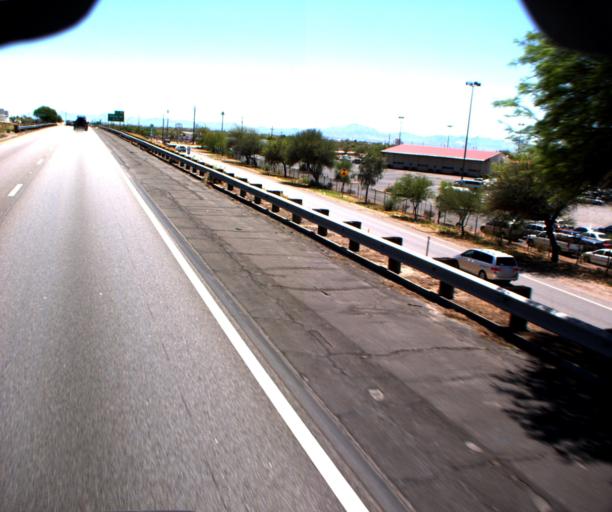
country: US
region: Arizona
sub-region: Pima County
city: Summit
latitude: 32.1263
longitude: -110.8771
